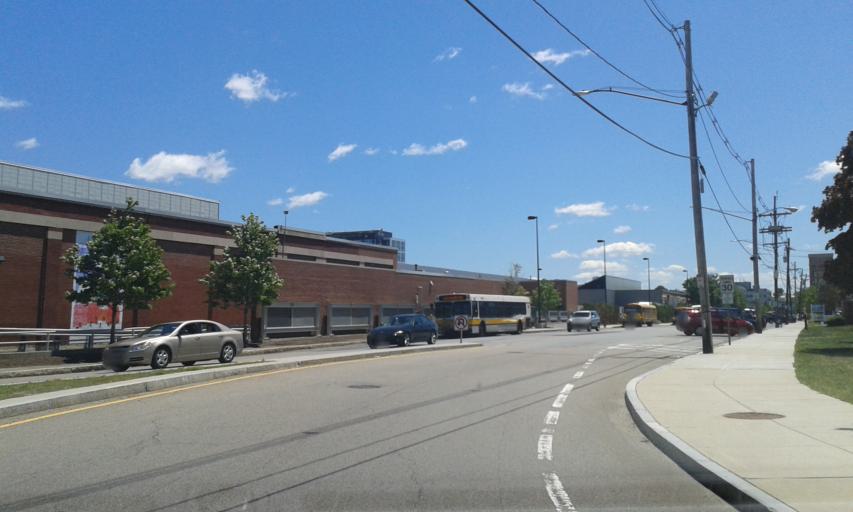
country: US
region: Massachusetts
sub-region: Middlesex County
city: Somerville
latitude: 42.3963
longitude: -71.0843
